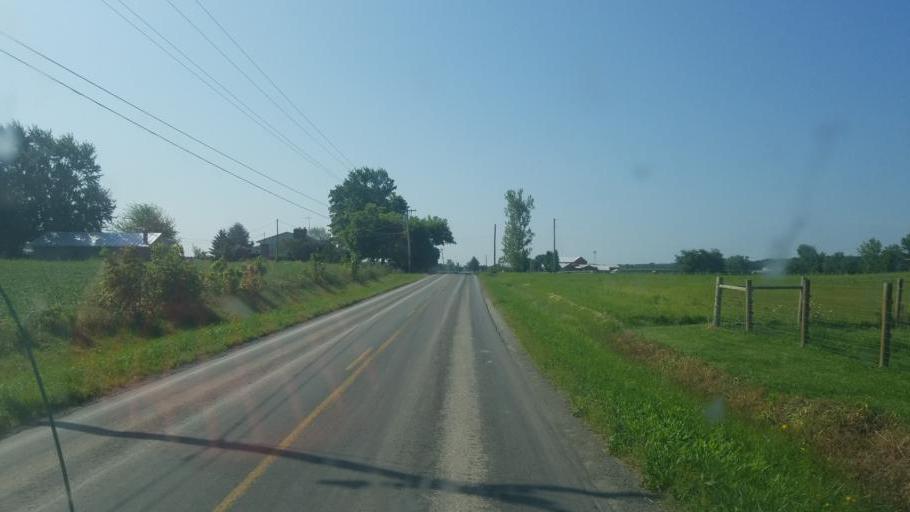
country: US
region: Ohio
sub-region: Wayne County
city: West Salem
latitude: 41.0093
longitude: -82.1640
